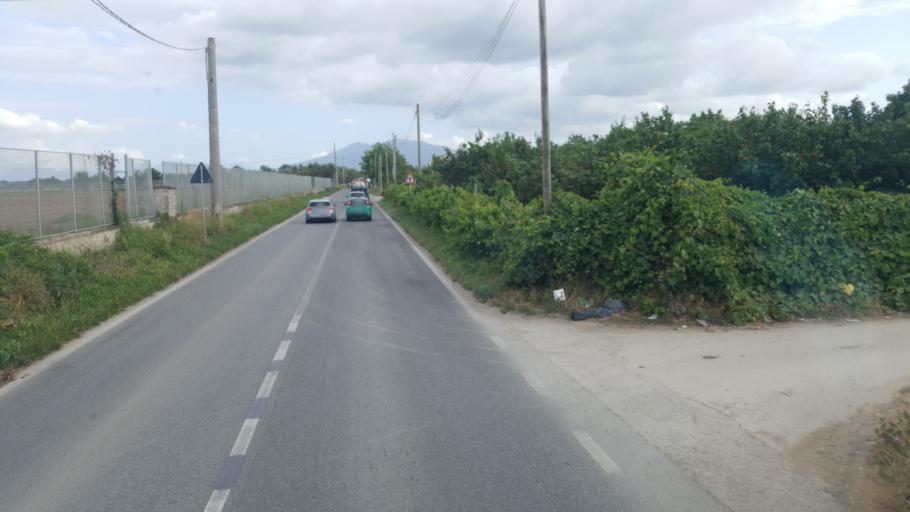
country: IT
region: Campania
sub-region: Provincia di Caserta
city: Montedecoro
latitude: 40.9990
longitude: 14.3949
